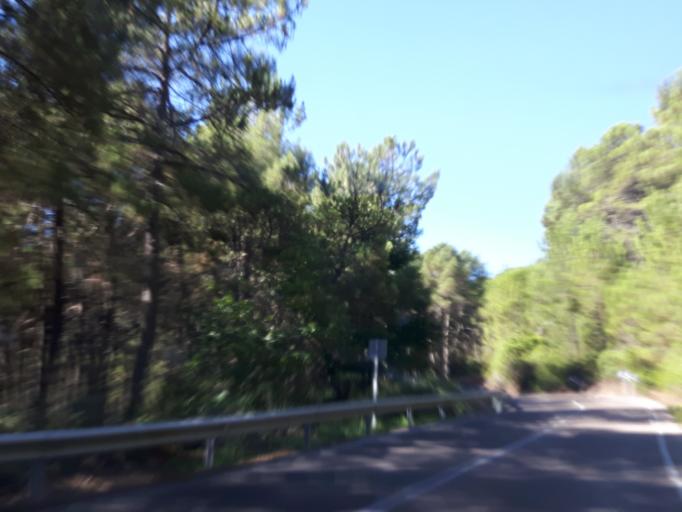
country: ES
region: Castille and Leon
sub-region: Provincia de Avila
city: Mombeltran
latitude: 40.2318
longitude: -5.0451
